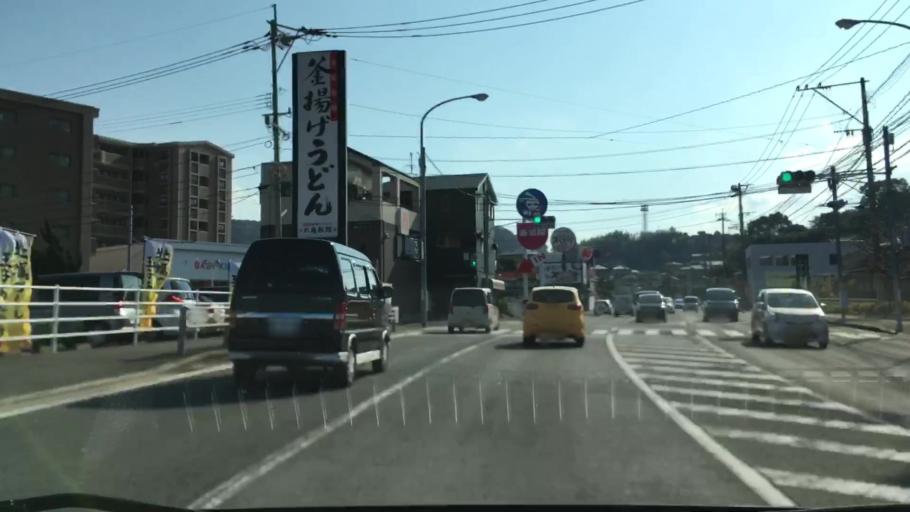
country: JP
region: Nagasaki
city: Togitsu
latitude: 32.8394
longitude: 129.8378
